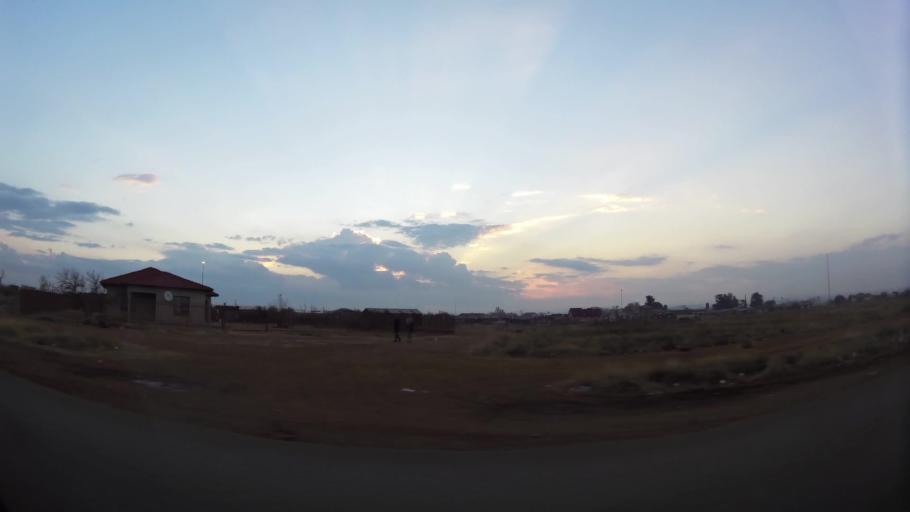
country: ZA
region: Gauteng
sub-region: City of Johannesburg Metropolitan Municipality
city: Orange Farm
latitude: -26.5539
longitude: 27.8807
